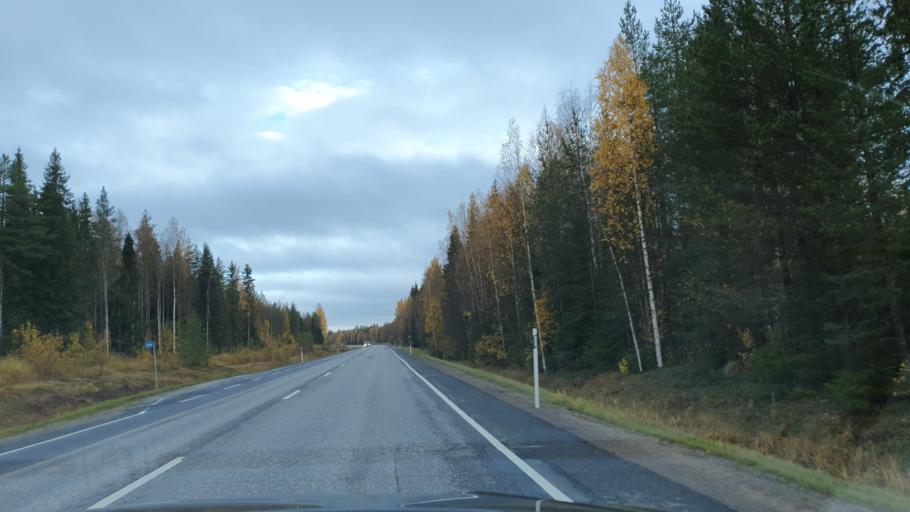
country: FI
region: Lapland
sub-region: Rovaniemi
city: Rovaniemi
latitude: 66.5695
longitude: 25.6365
